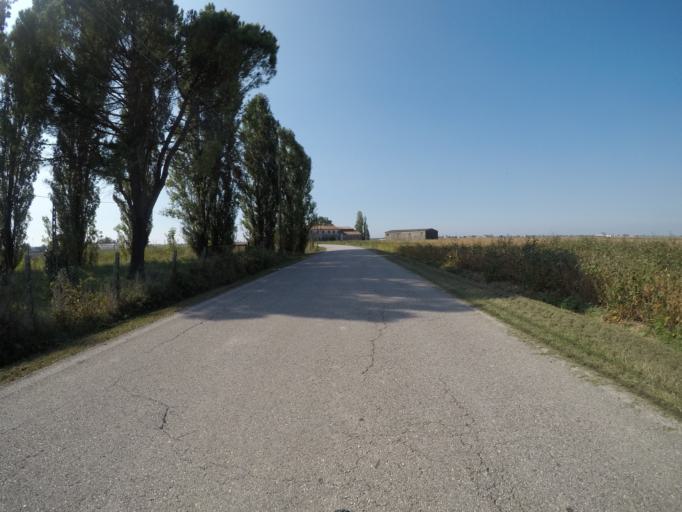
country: IT
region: Veneto
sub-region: Provincia di Rovigo
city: Polesella
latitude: 44.9763
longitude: 11.7239
